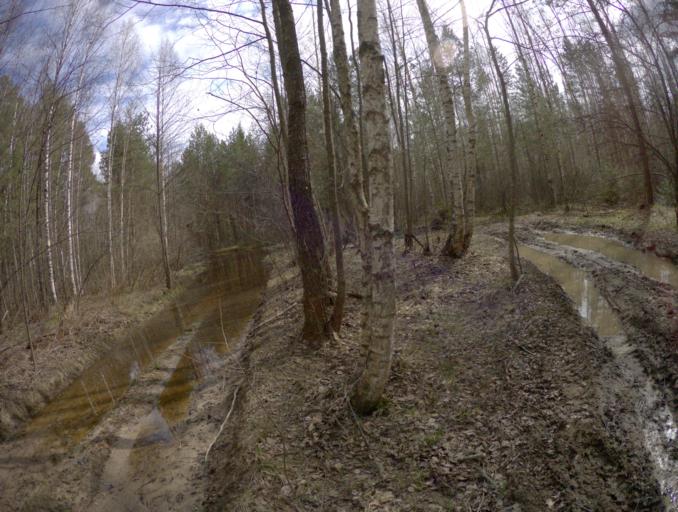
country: RU
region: Vladimir
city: Orgtrud
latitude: 56.0726
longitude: 40.7078
